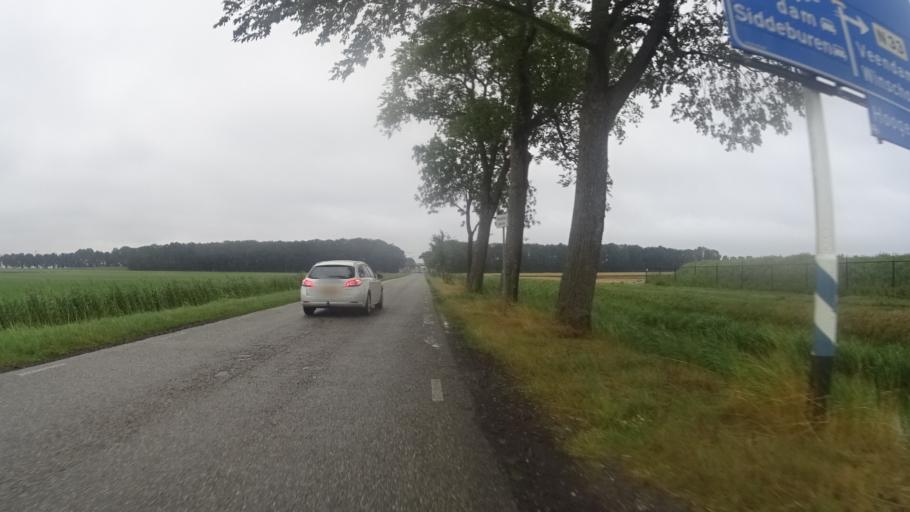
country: NL
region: Groningen
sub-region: Gemeente Veendam
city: Veendam
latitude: 53.1923
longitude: 6.8884
